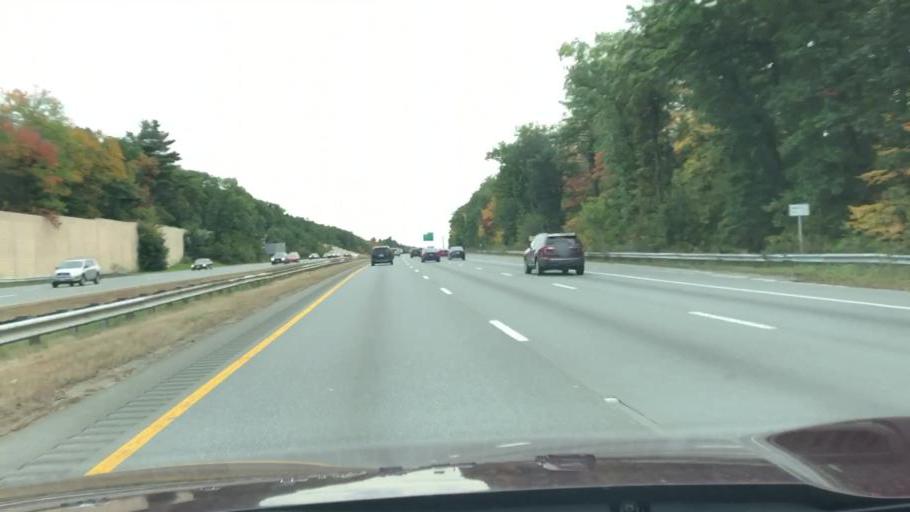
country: US
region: Massachusetts
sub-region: Essex County
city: Andover
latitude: 42.6368
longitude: -71.1820
